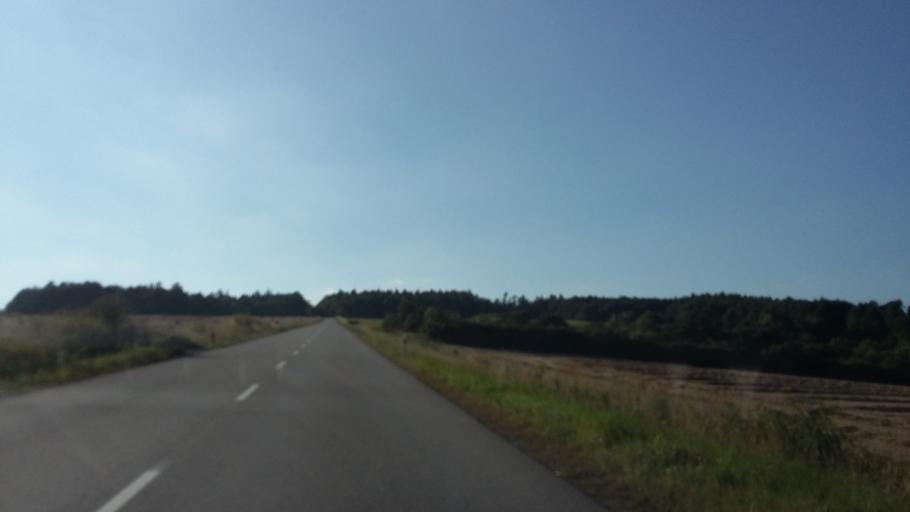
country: CZ
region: South Moravian
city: Ricany
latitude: 49.2165
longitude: 16.3815
